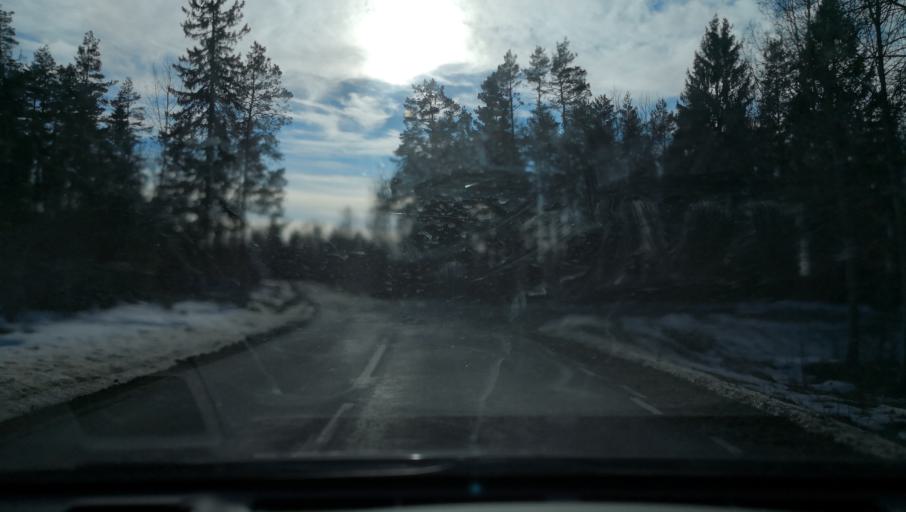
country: SE
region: Uppsala
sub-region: Osthammars Kommun
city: Osterbybruk
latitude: 60.2592
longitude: 17.9492
